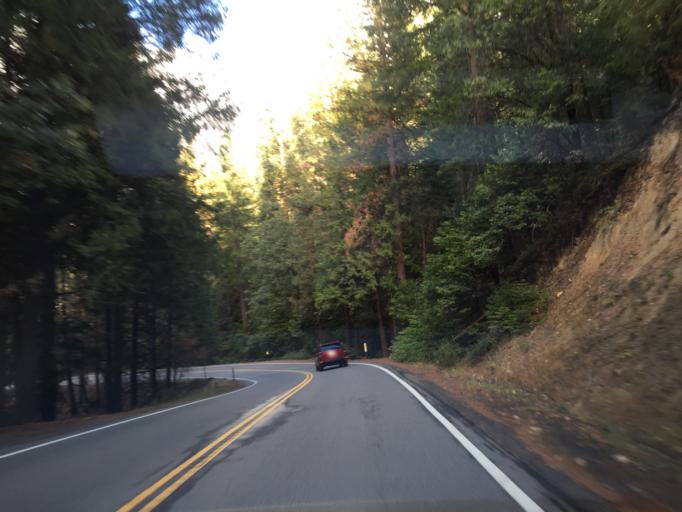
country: US
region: California
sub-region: Madera County
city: Ahwahnee
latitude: 37.5215
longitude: -119.6197
